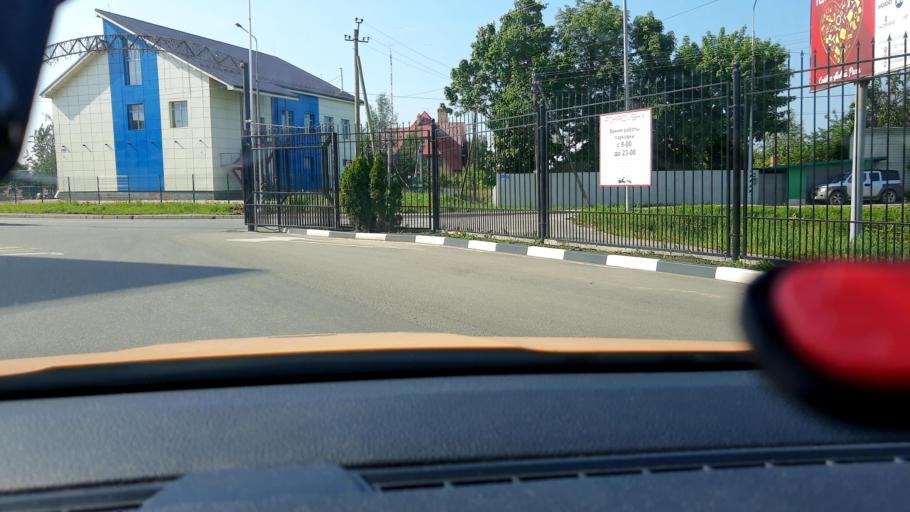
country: RU
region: Moskovskaya
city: Rozhdestveno
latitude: 55.8106
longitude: 37.0128
